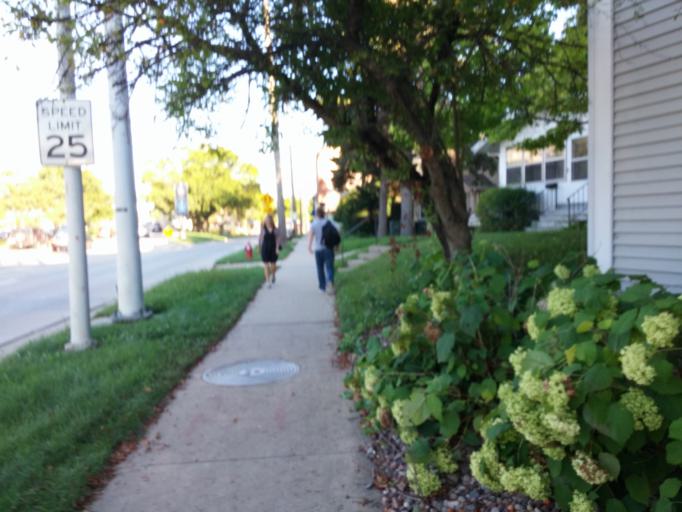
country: US
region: Wisconsin
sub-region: Dane County
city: Shorewood Hills
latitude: 43.0731
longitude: -89.4328
